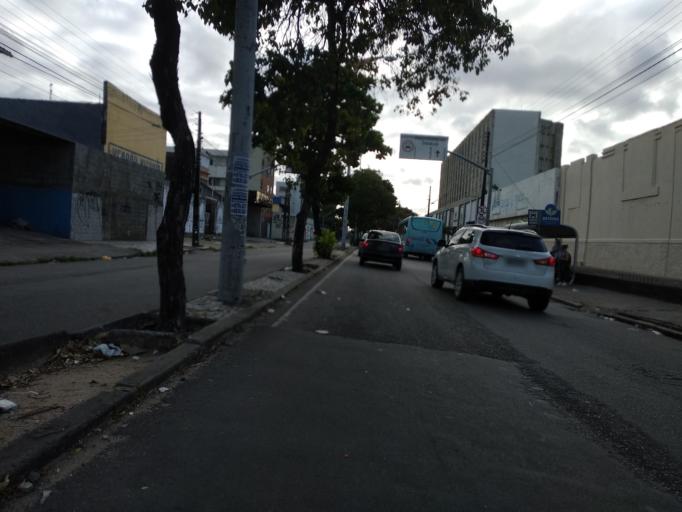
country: BR
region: Ceara
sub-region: Fortaleza
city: Fortaleza
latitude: -3.7294
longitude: -38.5371
